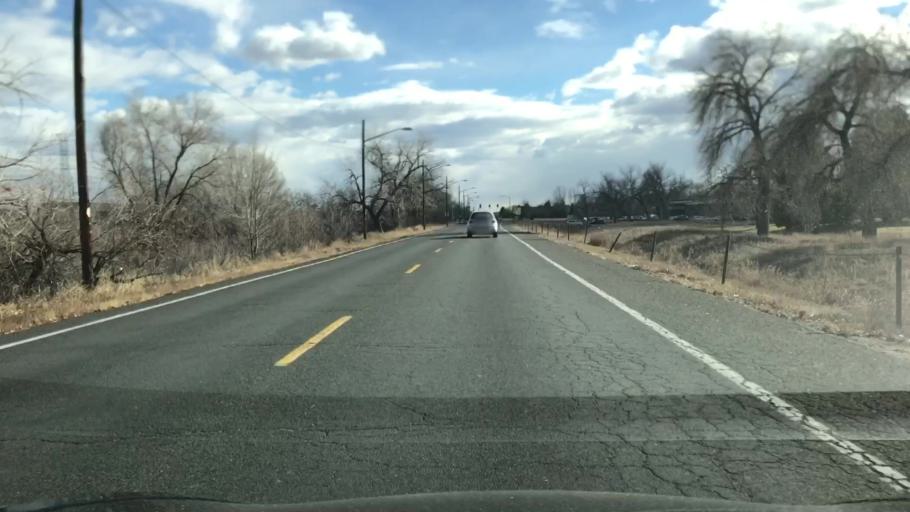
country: US
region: Colorado
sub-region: Arapahoe County
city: Glendale
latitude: 39.6894
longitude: -104.9110
